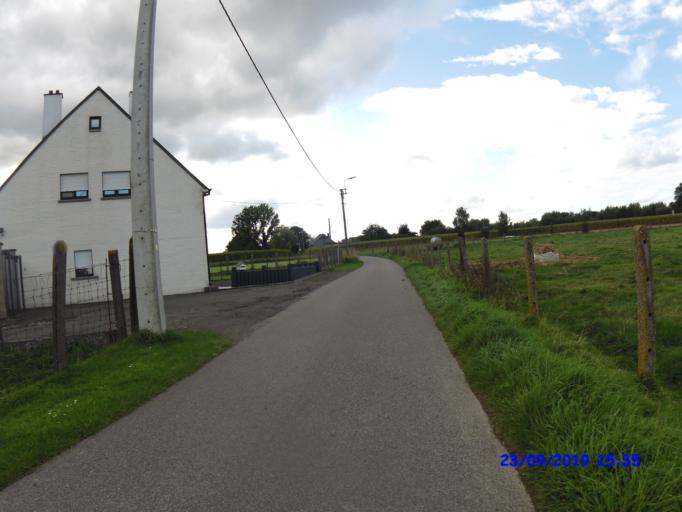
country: BE
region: Flanders
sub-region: Provincie Oost-Vlaanderen
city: Haaltert
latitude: 50.9117
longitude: 3.9443
